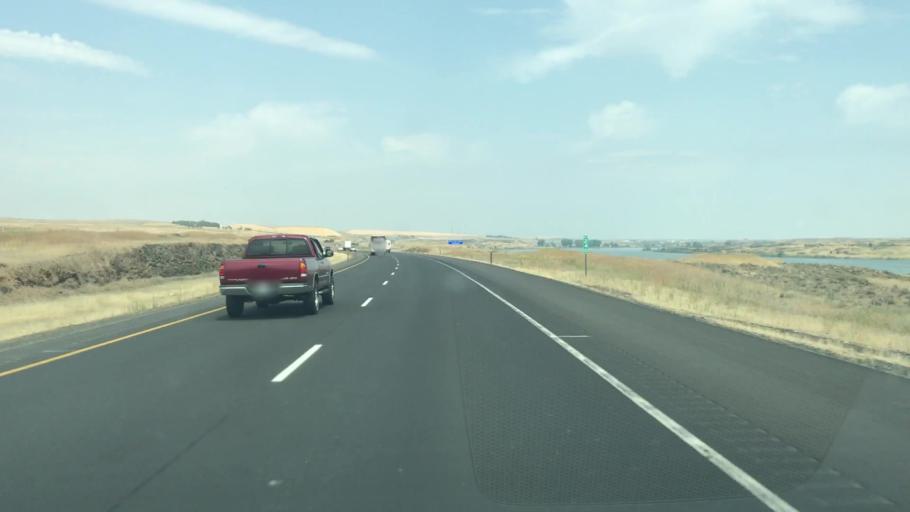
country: US
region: Washington
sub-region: Adams County
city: Ritzville
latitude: 47.2677
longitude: -118.0619
